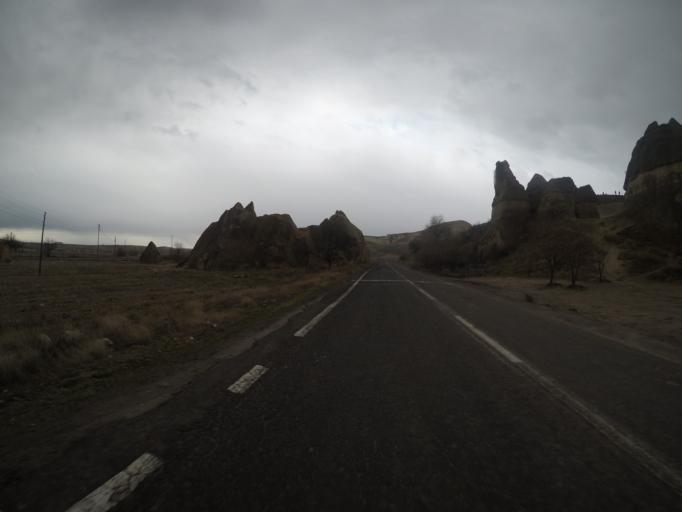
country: TR
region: Nevsehir
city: Avanos
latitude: 38.6777
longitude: 34.8568
